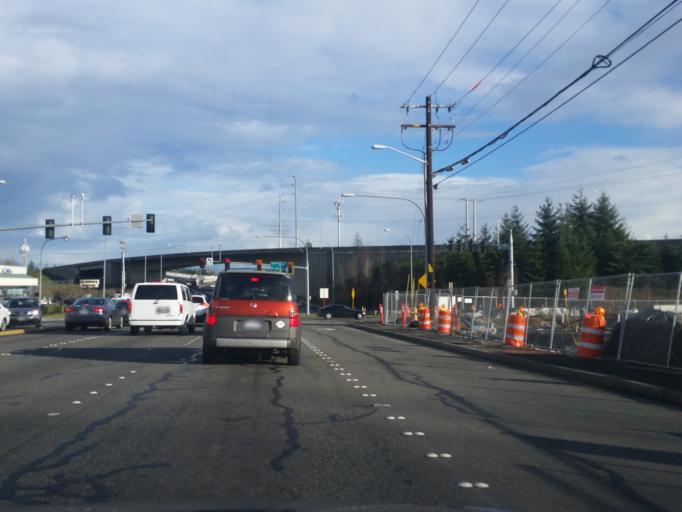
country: US
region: Washington
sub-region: Snohomish County
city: Alderwood Manor
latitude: 47.8209
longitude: -122.2840
